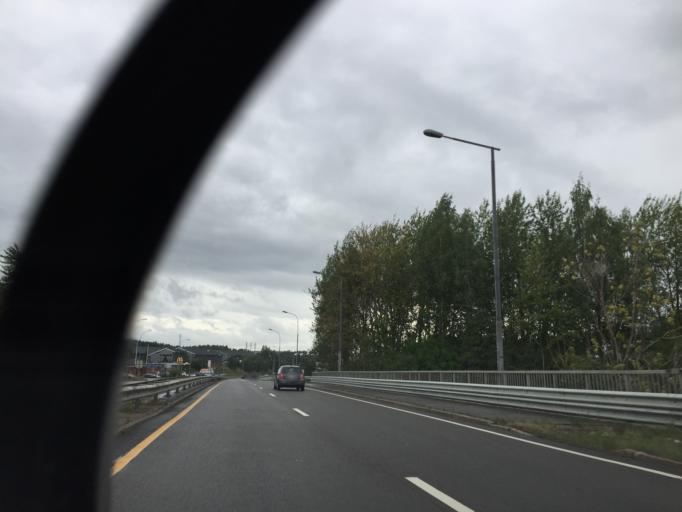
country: NO
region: Akershus
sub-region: Lorenskog
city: Kjenn
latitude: 59.9516
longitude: 10.8870
